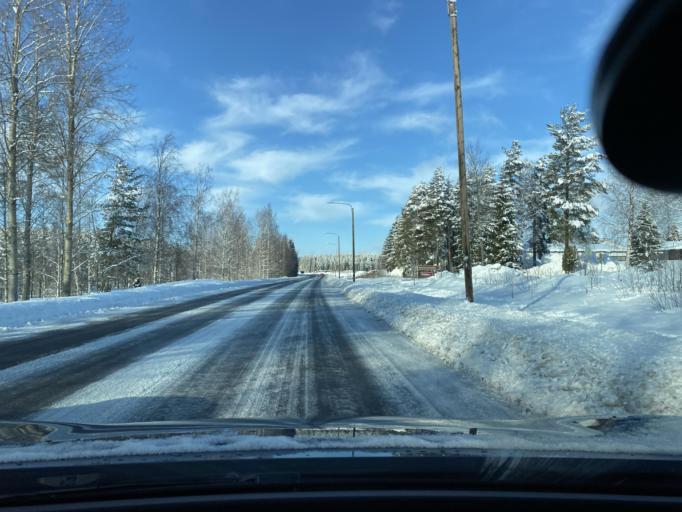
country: FI
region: Southern Savonia
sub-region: Mikkeli
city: Kangasniemi
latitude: 62.0073
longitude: 26.6427
